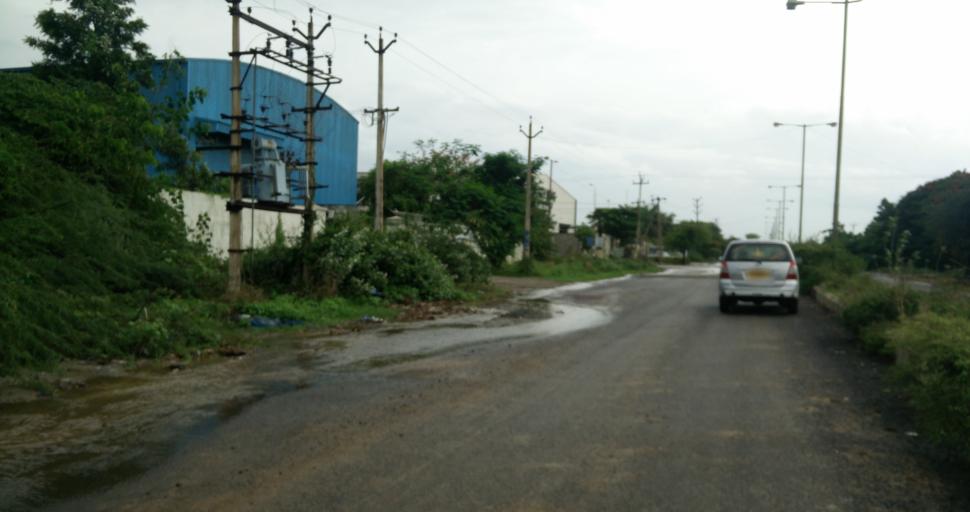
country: IN
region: Tamil Nadu
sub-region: Kancheepuram
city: Nandambakkam
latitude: 12.9996
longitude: 80.0261
